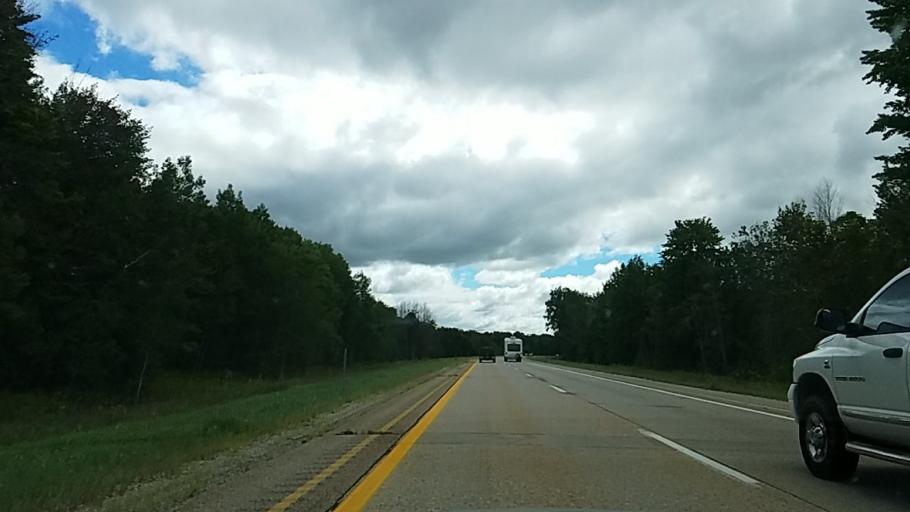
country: US
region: Michigan
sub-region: Ogemaw County
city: West Branch
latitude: 44.2108
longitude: -84.1977
